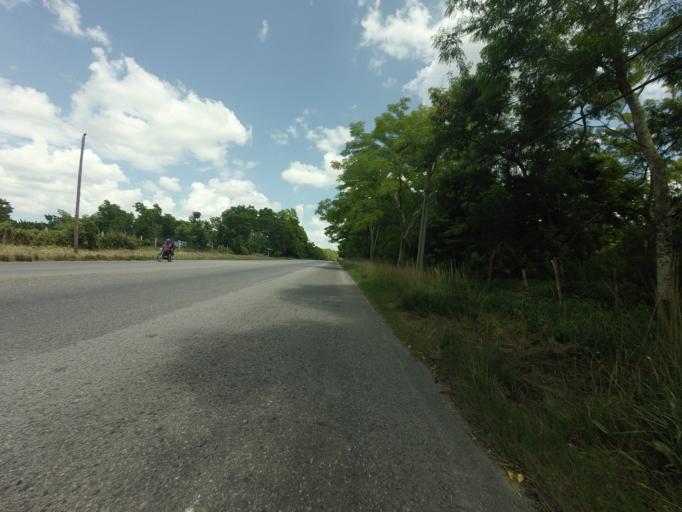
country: CU
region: La Habana
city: Arroyo Naranjo
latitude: 23.0371
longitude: -82.3431
